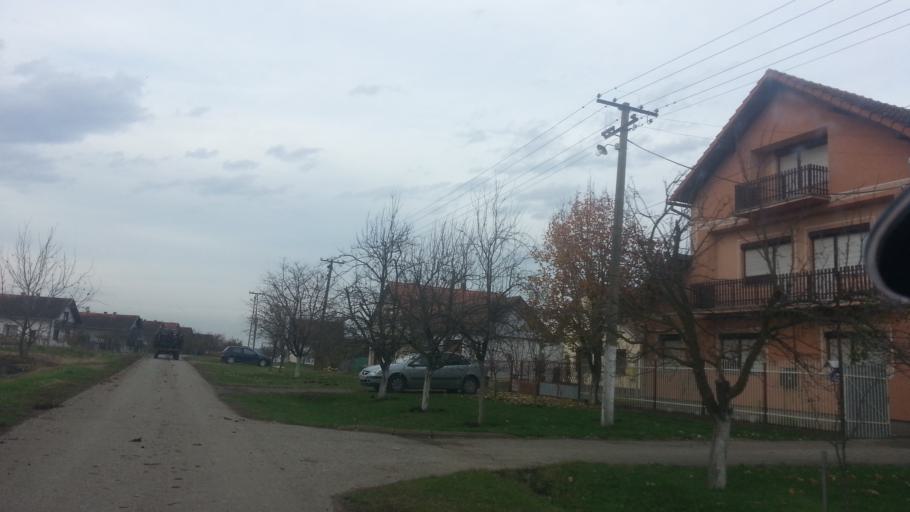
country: RS
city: Putinci
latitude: 44.9700
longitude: 19.9696
